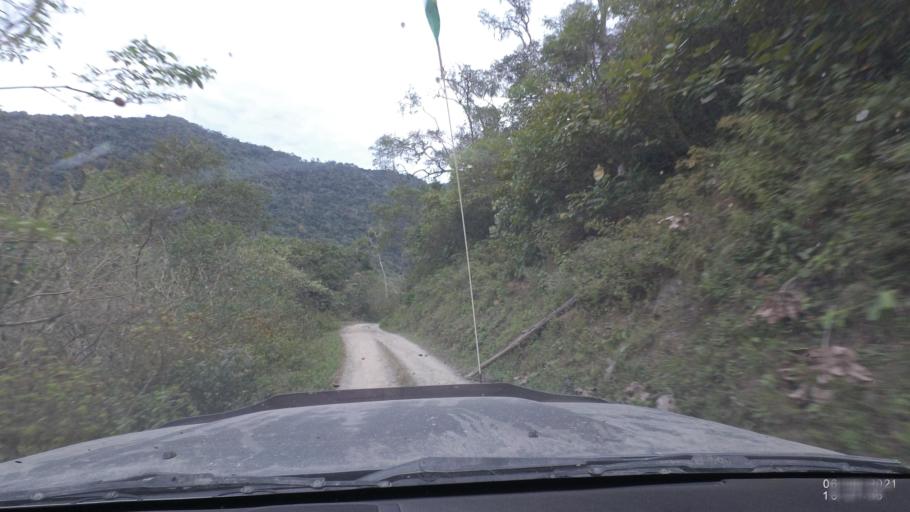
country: BO
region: La Paz
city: Quime
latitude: -16.5294
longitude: -66.7540
